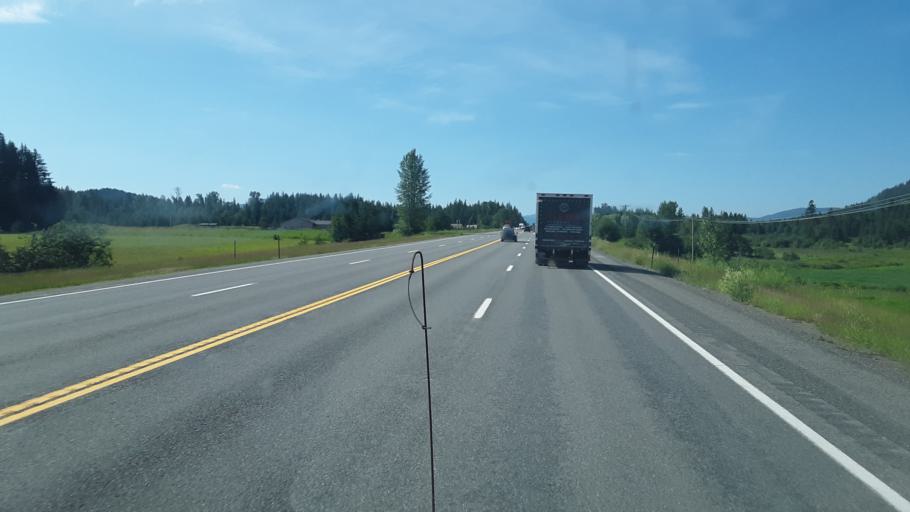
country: US
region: Idaho
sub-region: Bonner County
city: Ponderay
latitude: 48.3531
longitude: -116.5476
